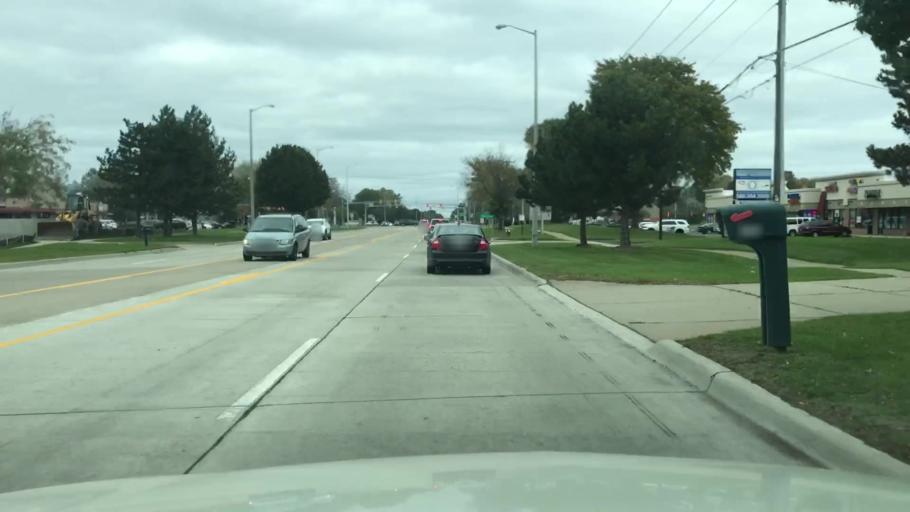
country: US
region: Michigan
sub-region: Macomb County
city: Sterling Heights
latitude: 42.5623
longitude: -83.0697
